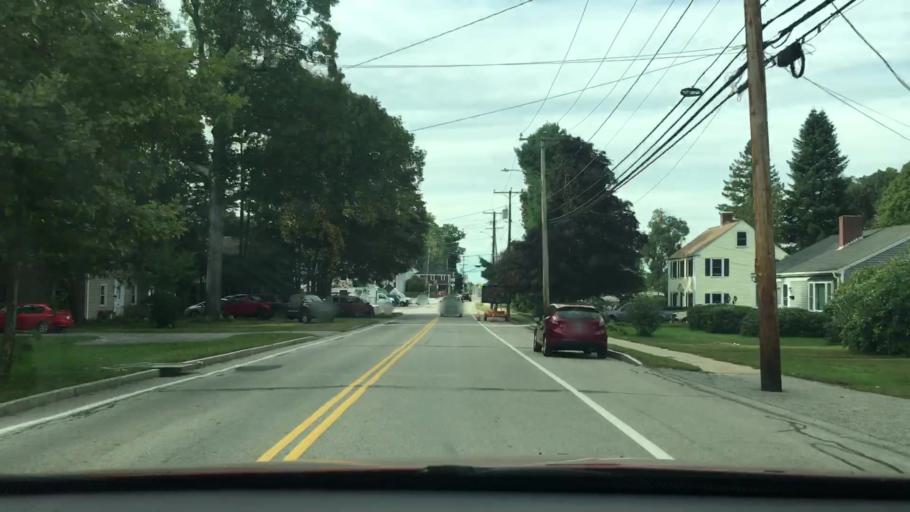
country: US
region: Maine
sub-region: York County
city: South Eliot
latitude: 43.0838
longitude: -70.7862
